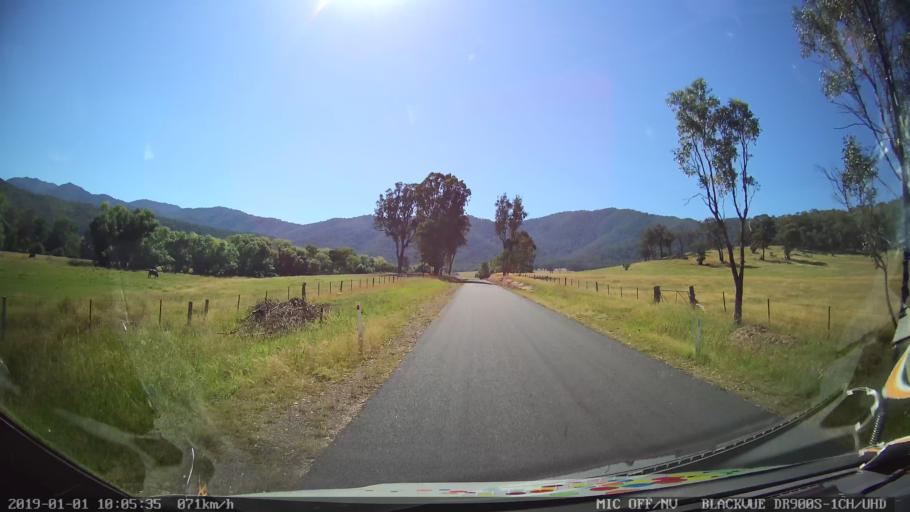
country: AU
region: New South Wales
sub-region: Snowy River
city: Jindabyne
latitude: -36.1739
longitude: 148.1378
